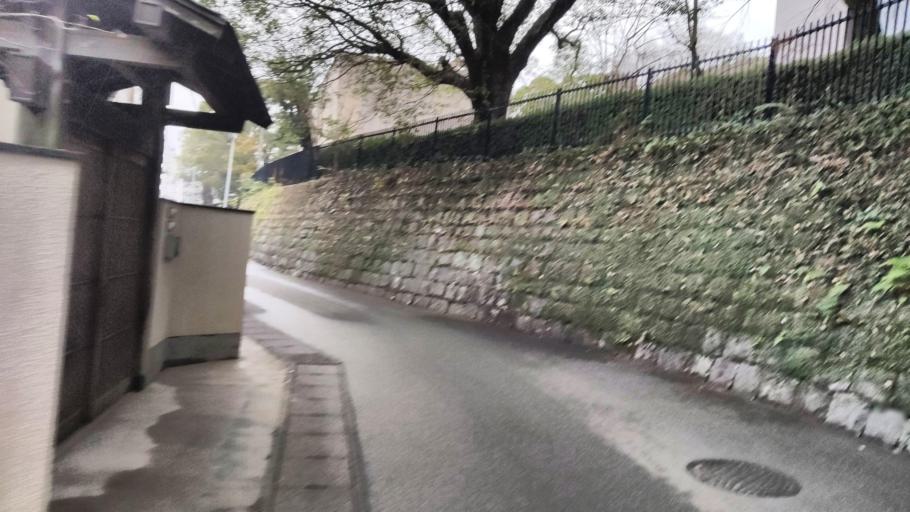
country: JP
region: Kumamoto
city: Kumamoto
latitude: 32.7855
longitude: 130.7357
